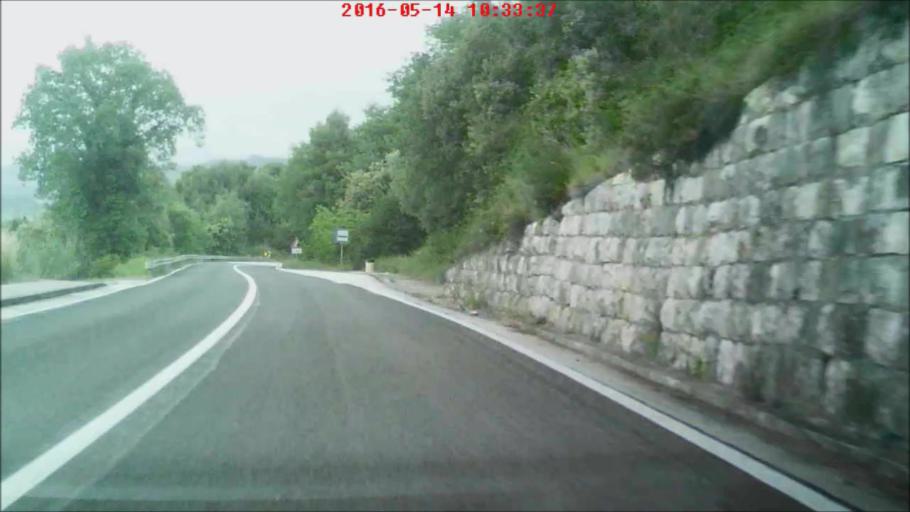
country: HR
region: Dubrovacko-Neretvanska
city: Podgora
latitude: 42.7750
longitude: 17.8881
